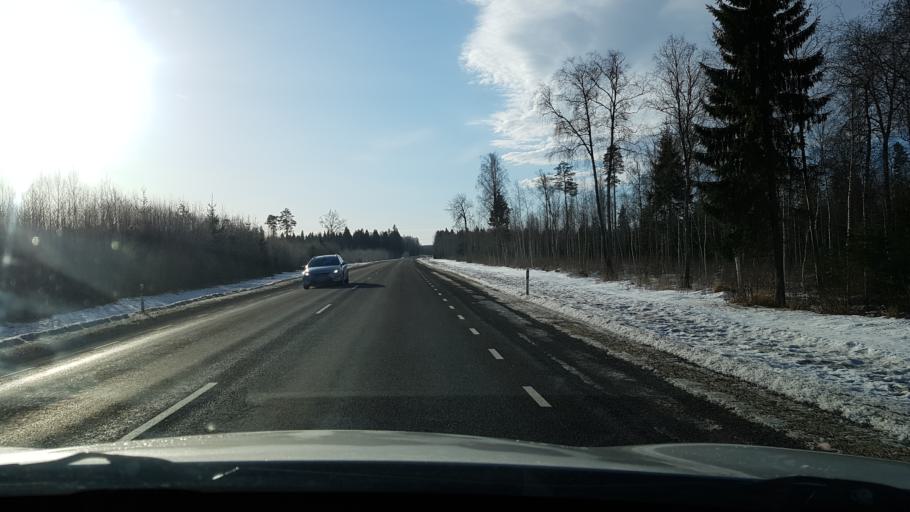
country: EE
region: Viljandimaa
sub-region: Vohma linn
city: Vohma
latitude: 58.6164
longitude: 25.5702
